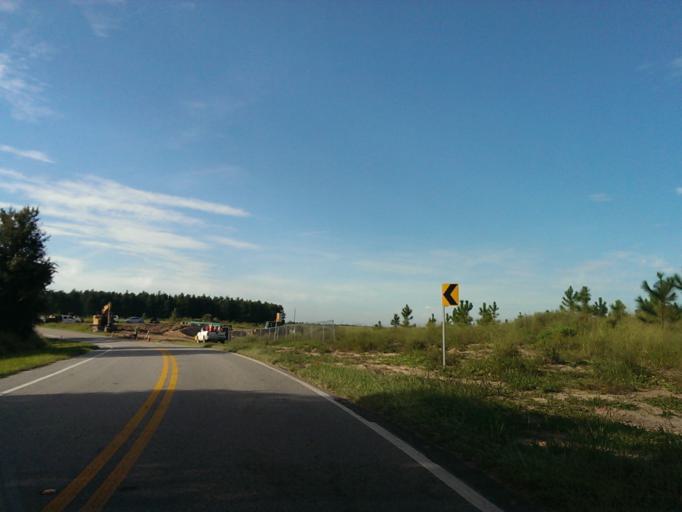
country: US
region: Florida
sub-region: Polk County
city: Citrus Ridge
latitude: 28.4269
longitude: -81.6189
